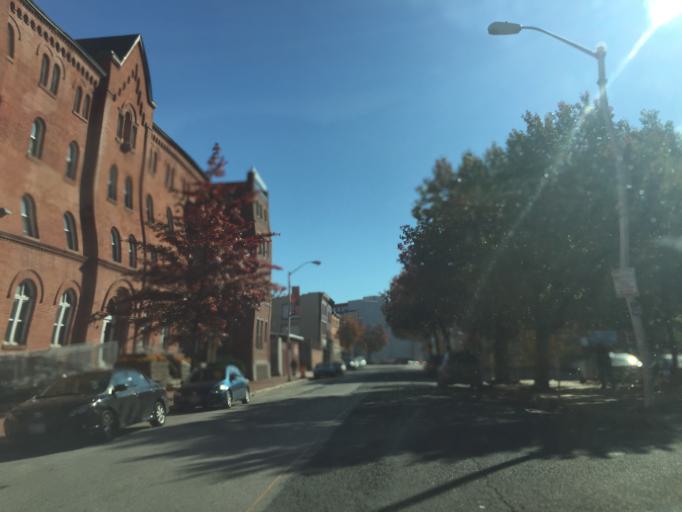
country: US
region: Maryland
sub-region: City of Baltimore
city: Baltimore
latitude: 39.2957
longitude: -76.6250
